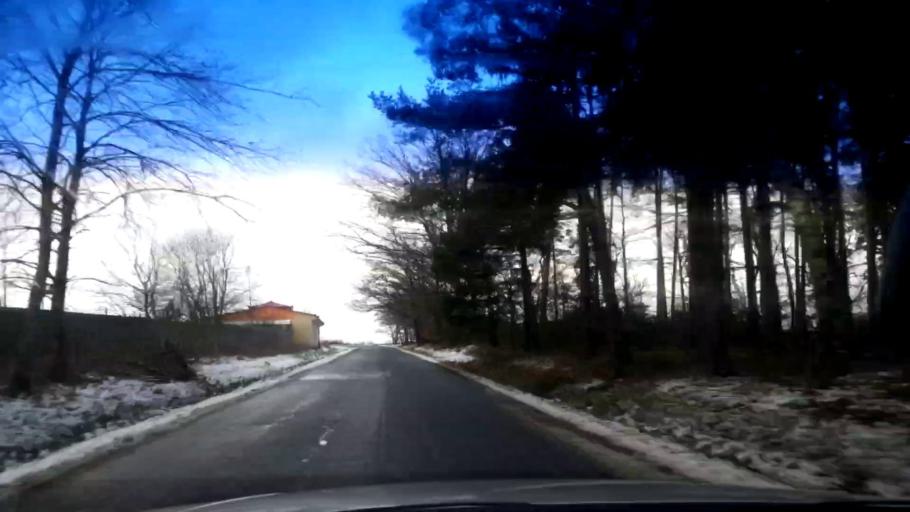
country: CZ
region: Karlovarsky
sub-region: Okres Cheb
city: Cheb
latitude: 50.0455
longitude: 12.3586
